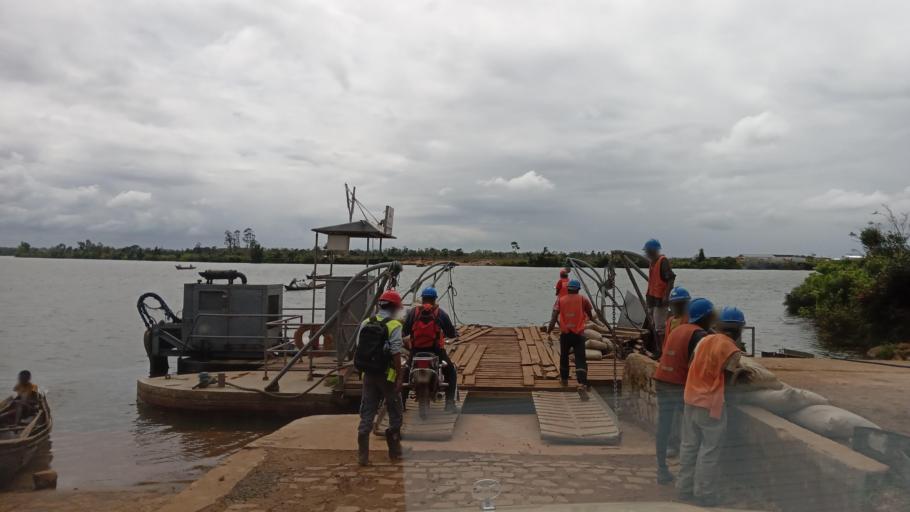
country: MG
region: Atsimo-Atsinanana
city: Vohipaho
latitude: -23.8153
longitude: 47.5490
